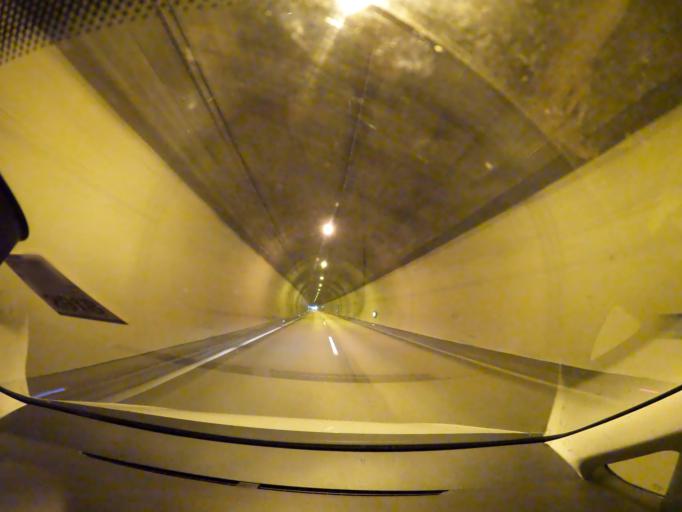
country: AT
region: Styria
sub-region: Politischer Bezirk Voitsberg
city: Pack
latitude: 46.9495
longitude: 15.0087
